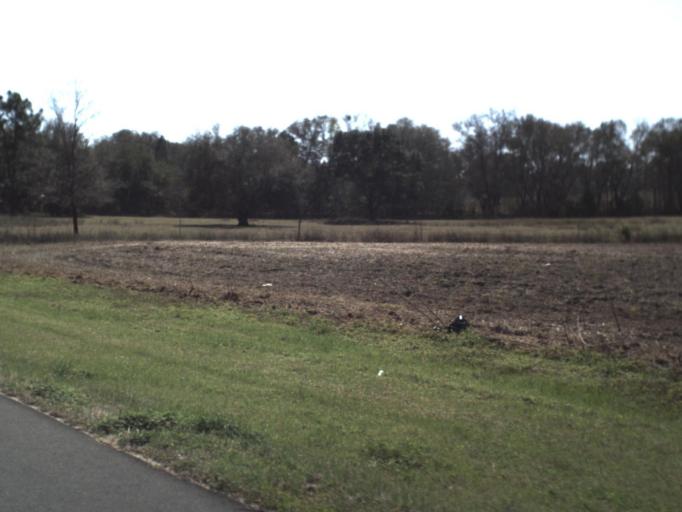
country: US
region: Florida
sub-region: Jackson County
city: Malone
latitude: 30.8421
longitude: -85.0658
